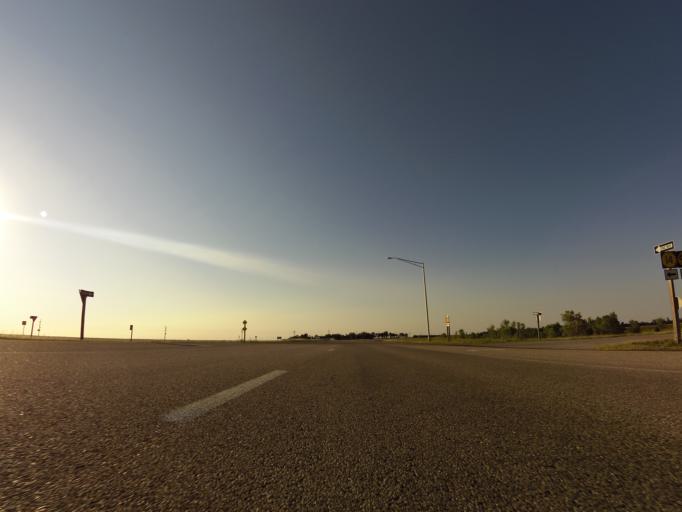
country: US
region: Kansas
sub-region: Reno County
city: South Hutchinson
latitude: 37.9737
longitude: -97.9381
